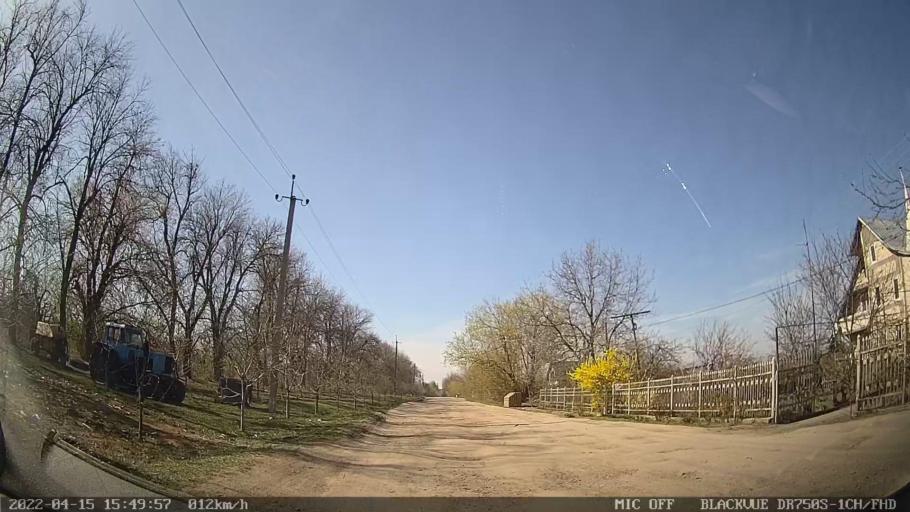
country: MD
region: Raionul Ocnita
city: Otaci
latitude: 48.3908
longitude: 27.9022
